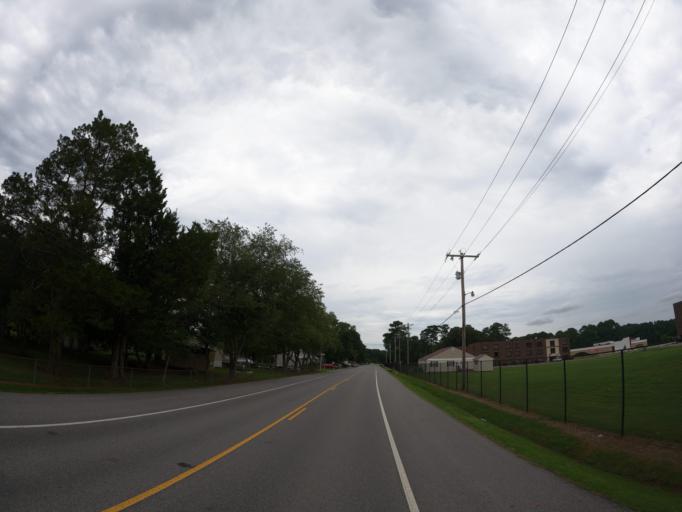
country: US
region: Maryland
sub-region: Saint Mary's County
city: Lexington Park
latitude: 38.1417
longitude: -76.5069
